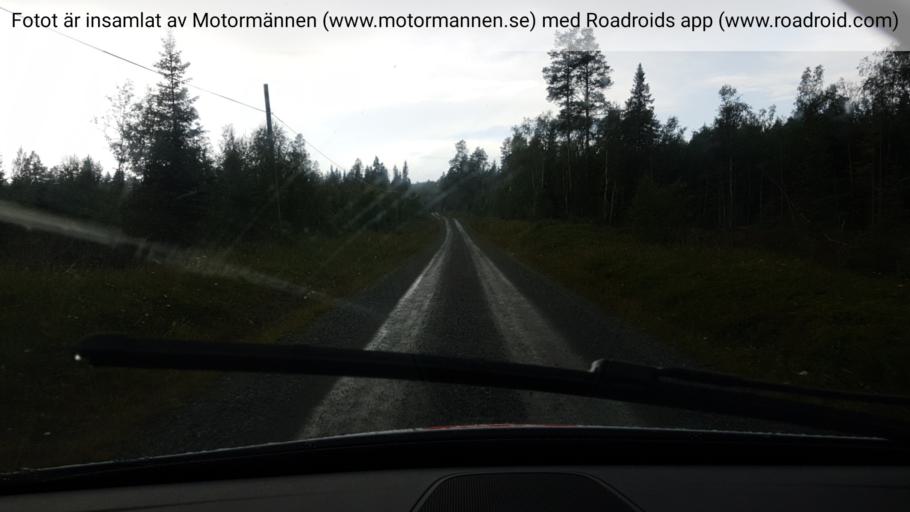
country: SE
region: Jaemtland
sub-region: OEstersunds Kommun
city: Brunflo
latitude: 63.0455
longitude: 14.7329
